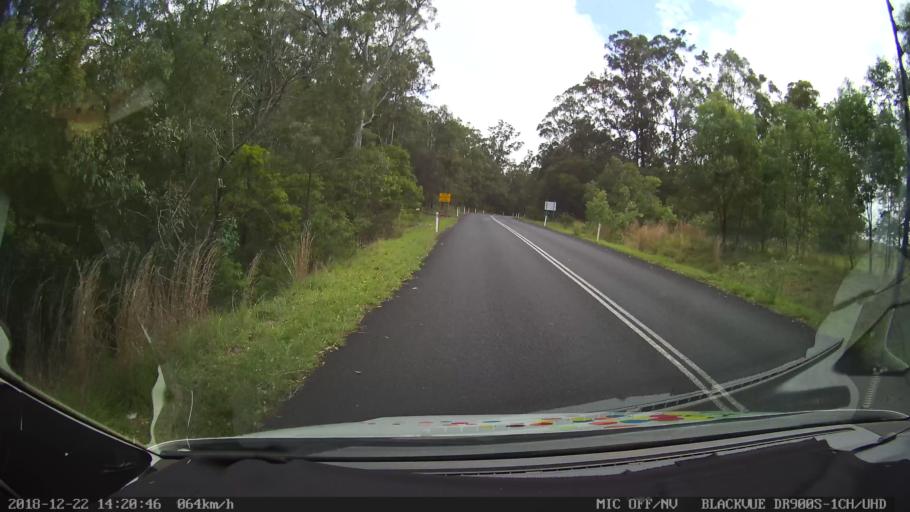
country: AU
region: New South Wales
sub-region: Clarence Valley
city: Coutts Crossing
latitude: -30.0170
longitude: 152.6640
